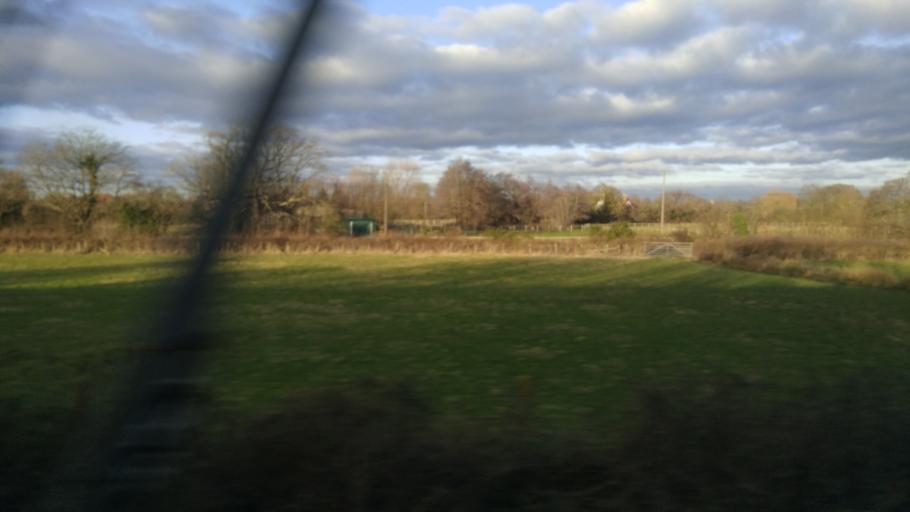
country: GB
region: England
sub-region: Kent
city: Headcorn
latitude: 51.1640
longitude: 0.6497
